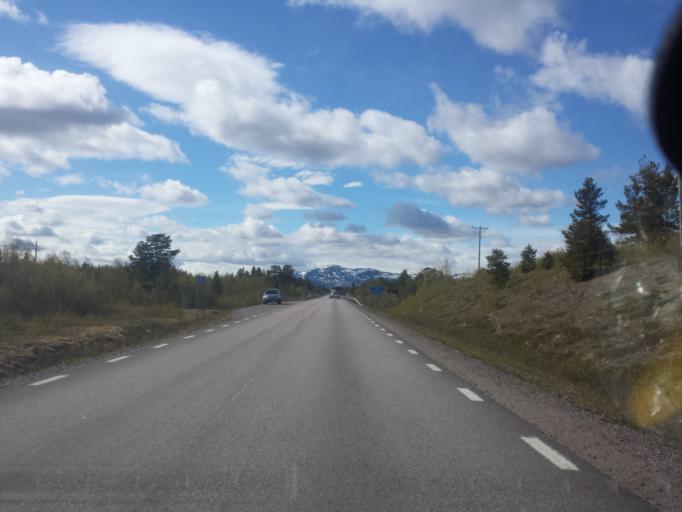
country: SE
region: Norrbotten
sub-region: Kiruna Kommun
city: Kiruna
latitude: 67.9897
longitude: 19.9278
